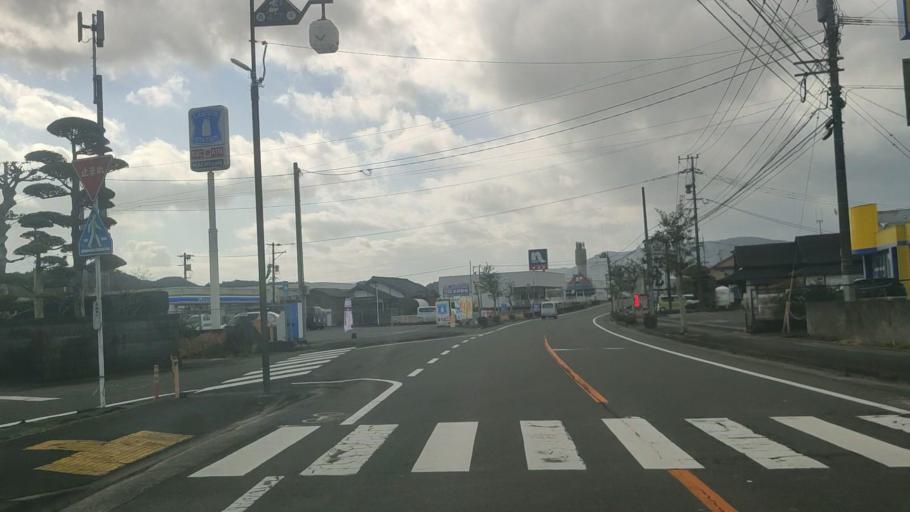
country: JP
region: Kagoshima
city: Okuchi-shinohara
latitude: 32.0499
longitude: 130.7733
